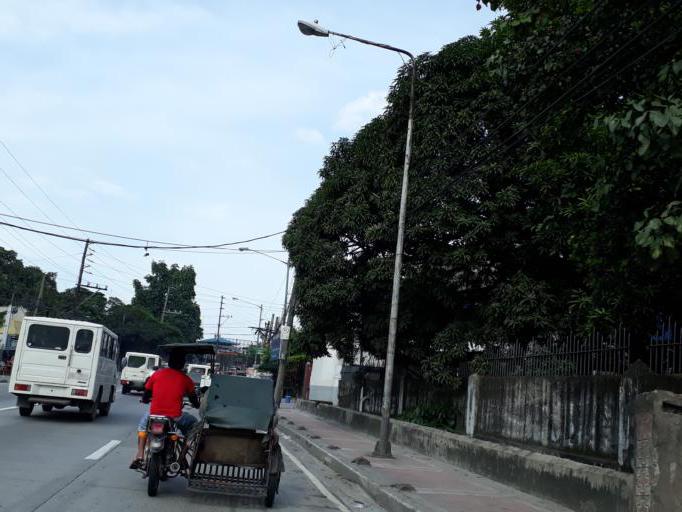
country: PH
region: Calabarzon
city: Del Monte
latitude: 14.6655
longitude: 121.0055
